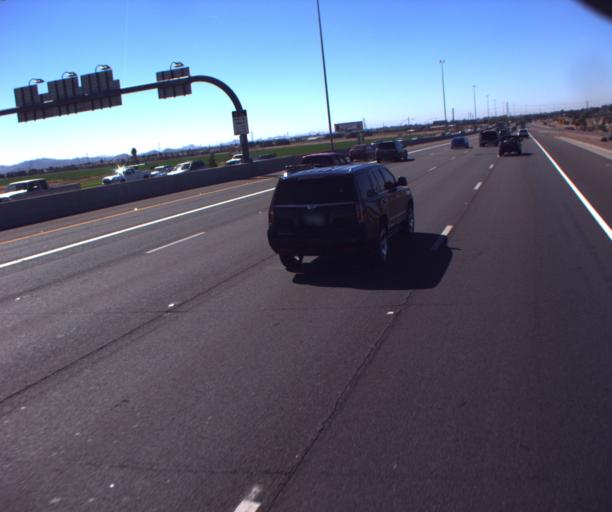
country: US
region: Arizona
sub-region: Maricopa County
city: Avondale
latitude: 33.4593
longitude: -112.3078
